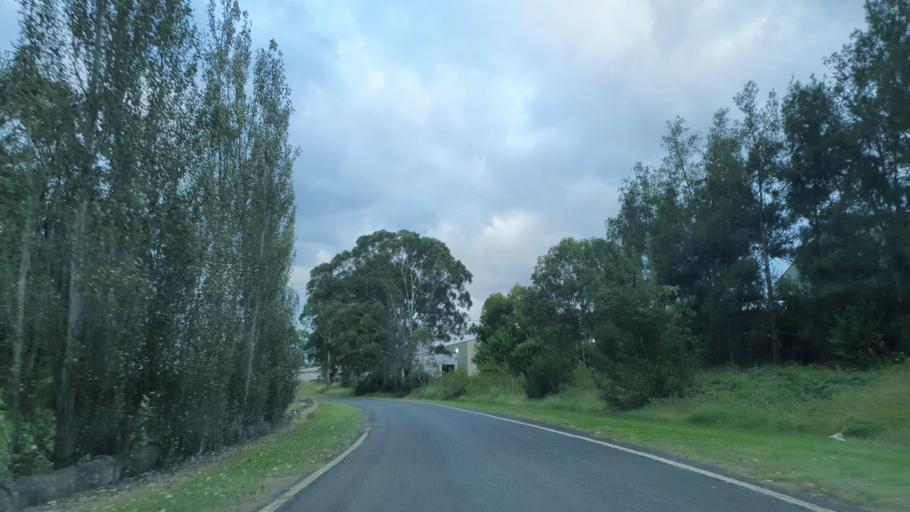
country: AU
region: New South Wales
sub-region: Penrith Municipality
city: Werrington County
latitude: -33.7425
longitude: 150.7631
